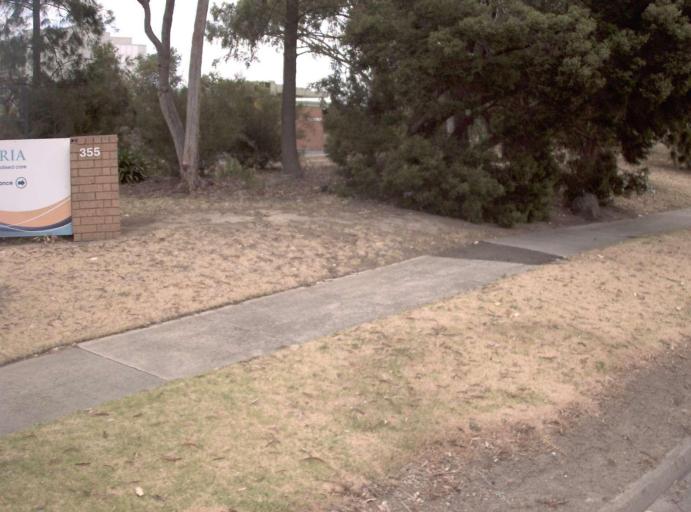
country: AU
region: Victoria
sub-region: Knox
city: Wantirna South
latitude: -37.8704
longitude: 145.2341
